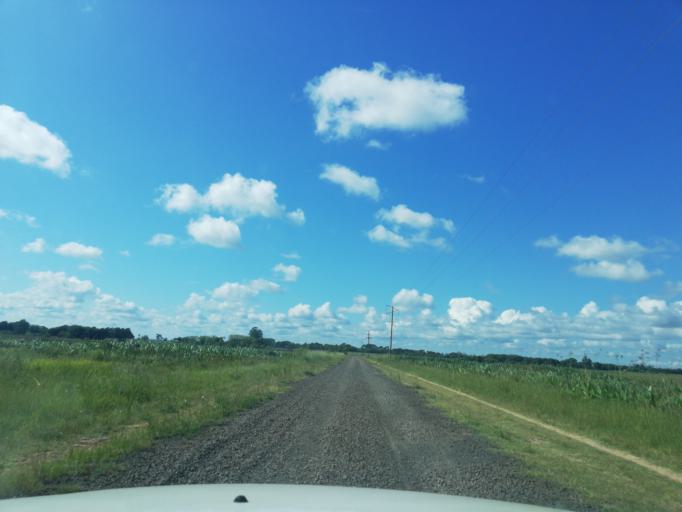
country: AR
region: Corrientes
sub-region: Departamento de San Miguel
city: San Miguel
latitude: -27.9757
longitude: -57.5809
